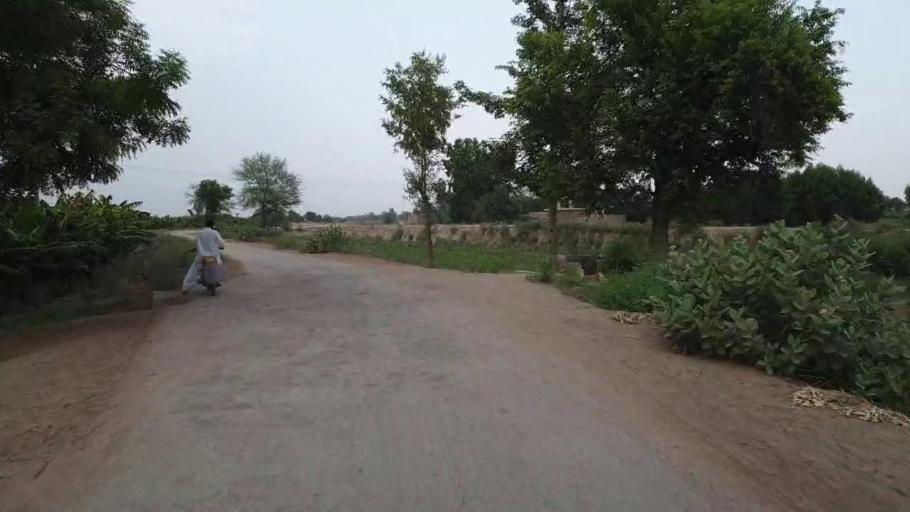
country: PK
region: Sindh
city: Bandhi
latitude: 26.5328
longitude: 68.2011
